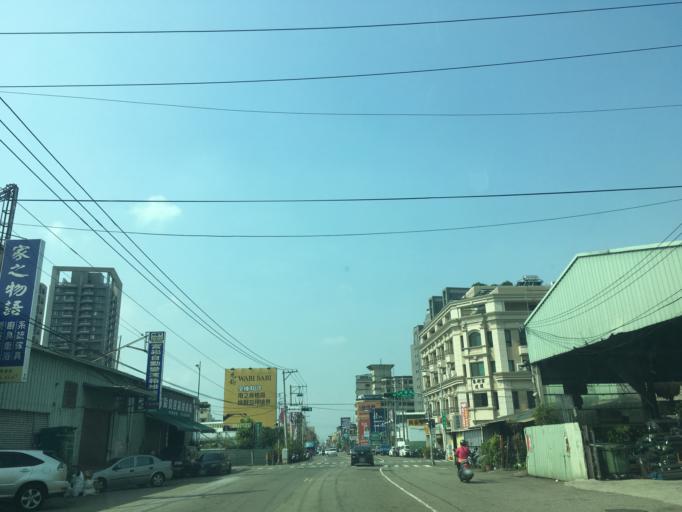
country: TW
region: Taiwan
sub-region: Taichung City
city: Taichung
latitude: 24.1614
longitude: 120.7137
